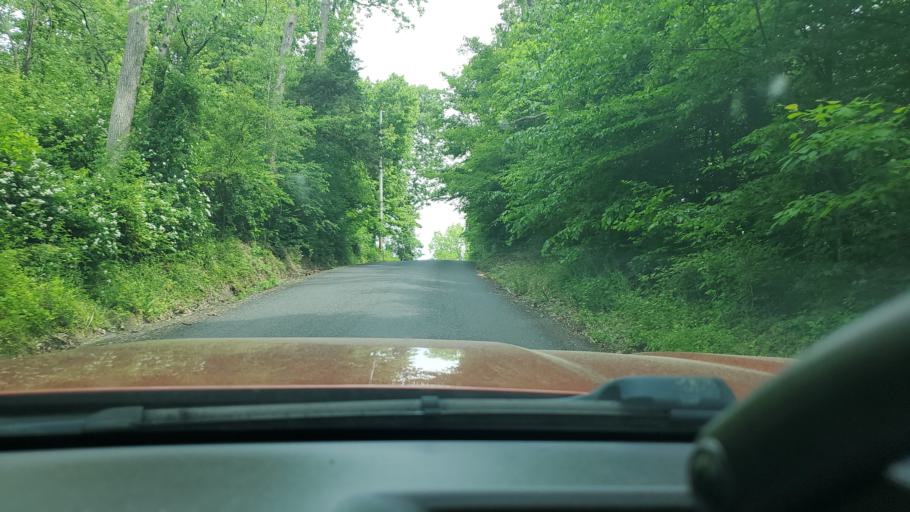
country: US
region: Pennsylvania
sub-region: Montgomery County
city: Red Hill
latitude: 40.3441
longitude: -75.5093
